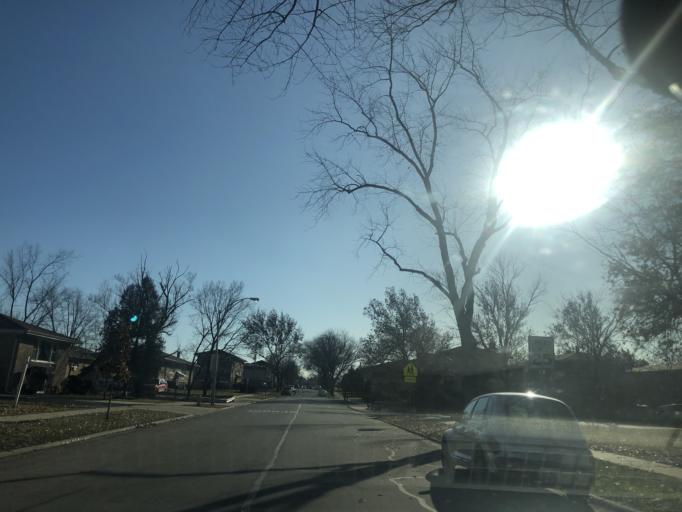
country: US
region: Illinois
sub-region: DuPage County
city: Addison
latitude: 41.9387
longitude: -87.9954
